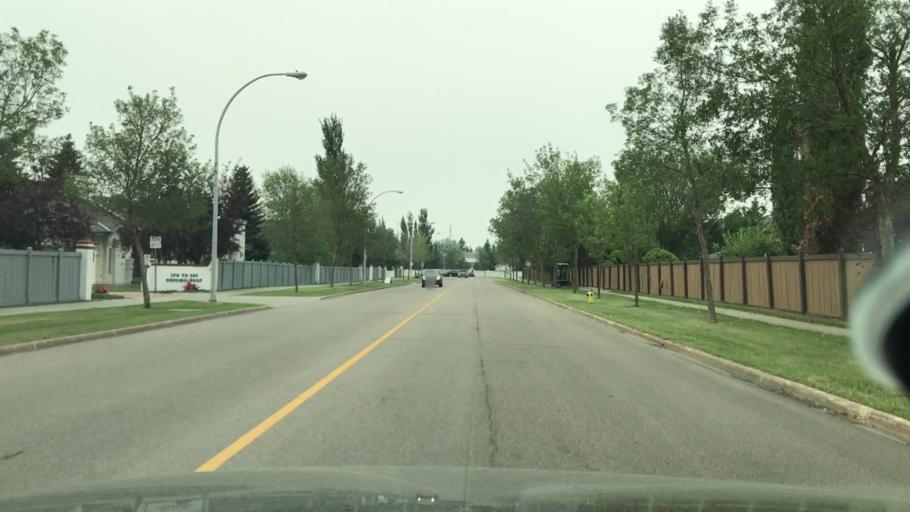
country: CA
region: Alberta
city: Edmonton
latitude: 53.4683
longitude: -113.5732
